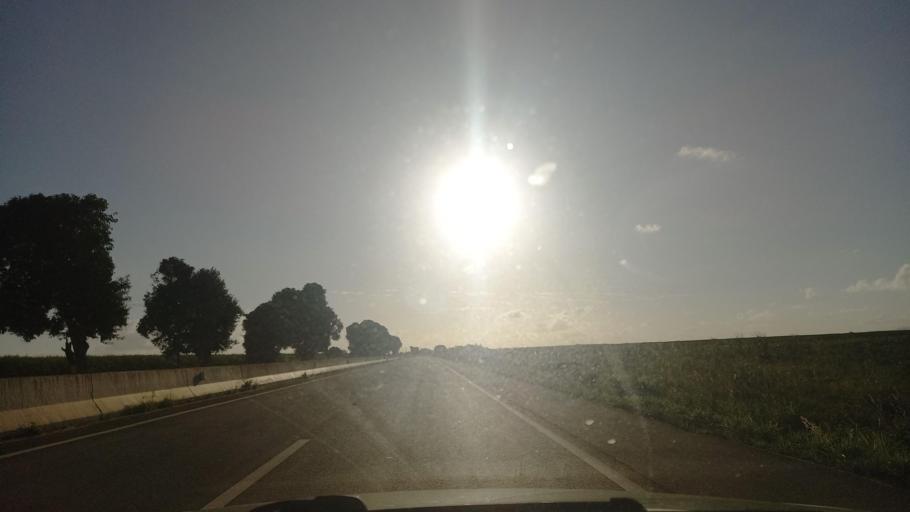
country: BR
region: Alagoas
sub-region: Campo Alegre
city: Campo Alegre
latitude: -9.7945
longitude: -36.3093
